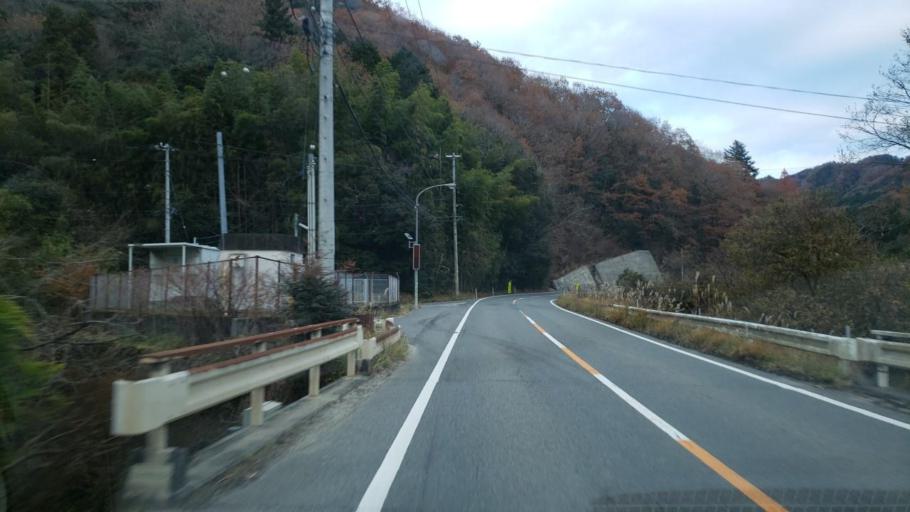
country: JP
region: Tokushima
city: Wakimachi
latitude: 34.1886
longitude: 134.1712
